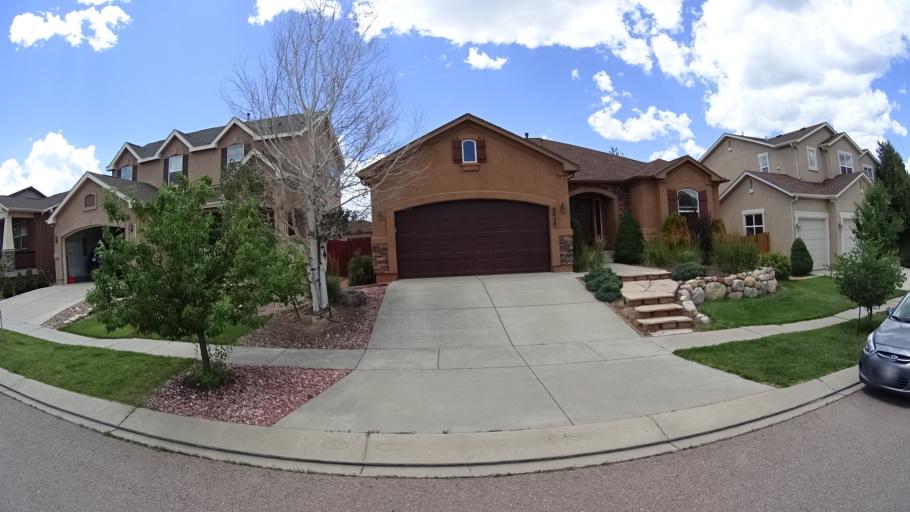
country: US
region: Colorado
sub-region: El Paso County
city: Black Forest
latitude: 38.9486
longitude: -104.7130
